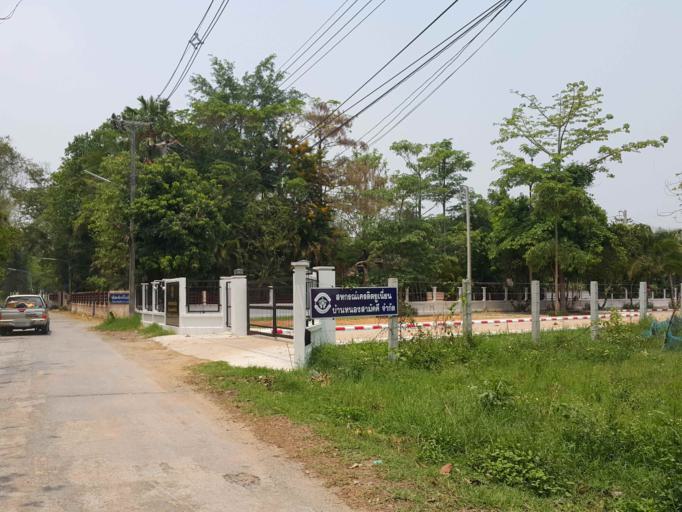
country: TH
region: Chiang Mai
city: San Sai
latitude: 18.8951
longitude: 99.0753
